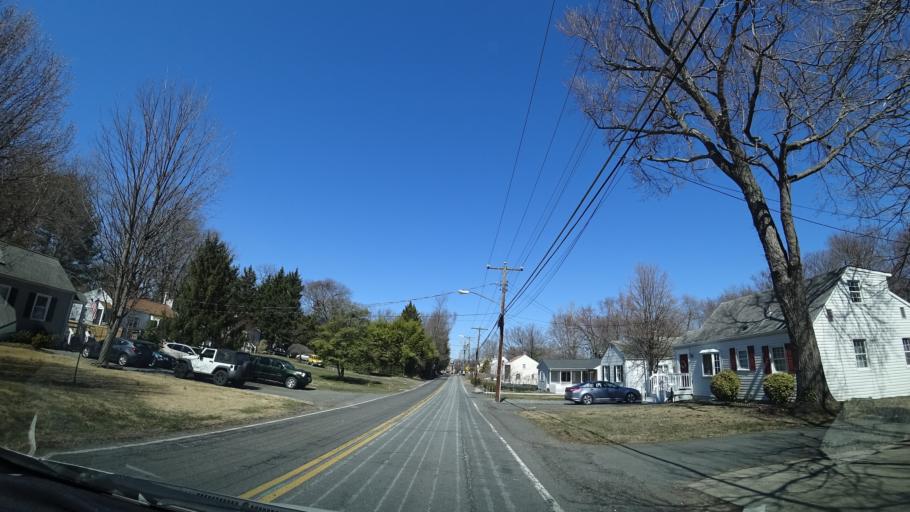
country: US
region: Virginia
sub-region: City of Fairfax
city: Fairfax
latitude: 38.8422
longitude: -77.2967
